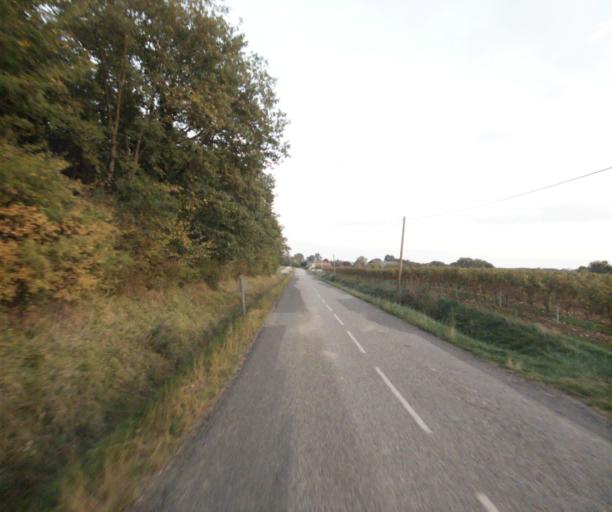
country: FR
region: Midi-Pyrenees
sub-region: Departement du Gers
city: Vic-Fezensac
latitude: 43.8003
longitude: 0.2344
